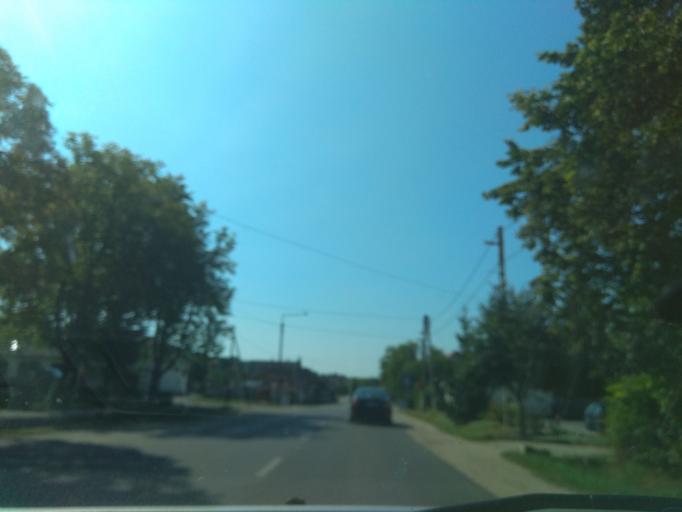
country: HU
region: Borsod-Abauj-Zemplen
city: Harsany
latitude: 47.9651
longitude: 20.7426
